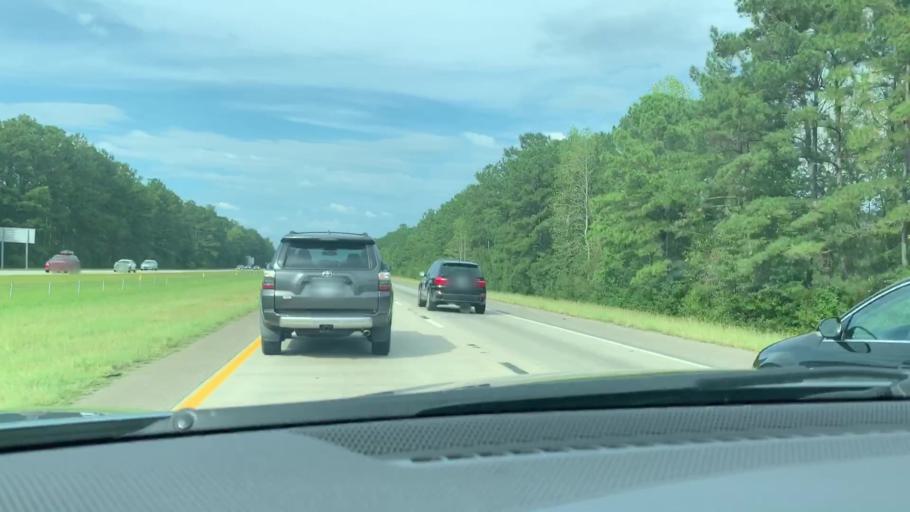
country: US
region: South Carolina
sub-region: Colleton County
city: Walterboro
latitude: 32.9475
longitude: -80.6829
